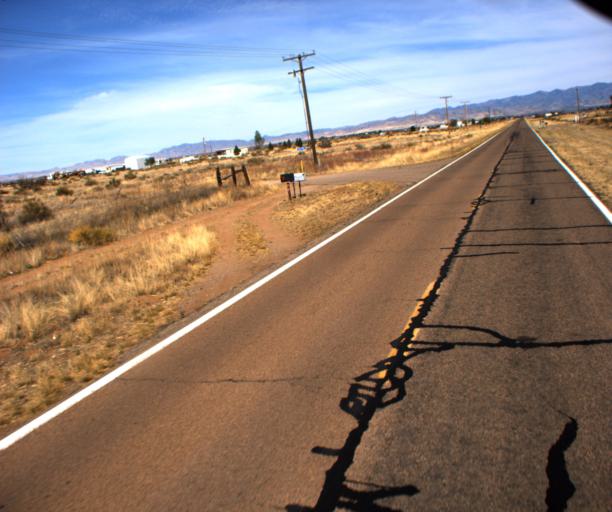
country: US
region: Arizona
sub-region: Cochise County
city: Willcox
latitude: 31.8837
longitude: -109.6841
